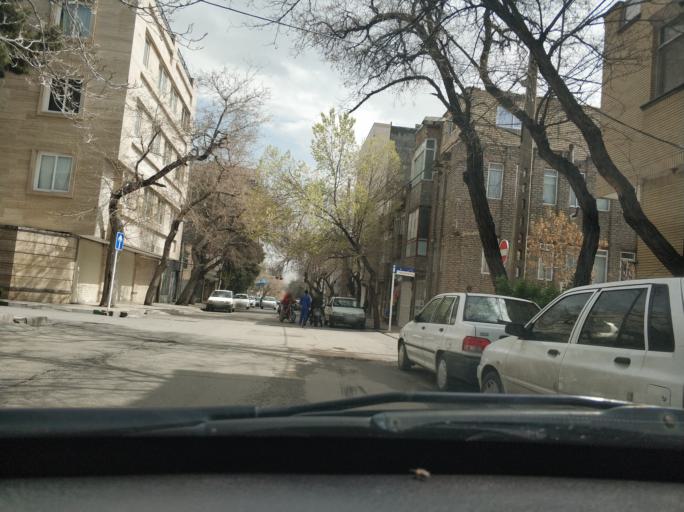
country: IR
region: Razavi Khorasan
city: Mashhad
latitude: 36.2789
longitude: 59.5732
